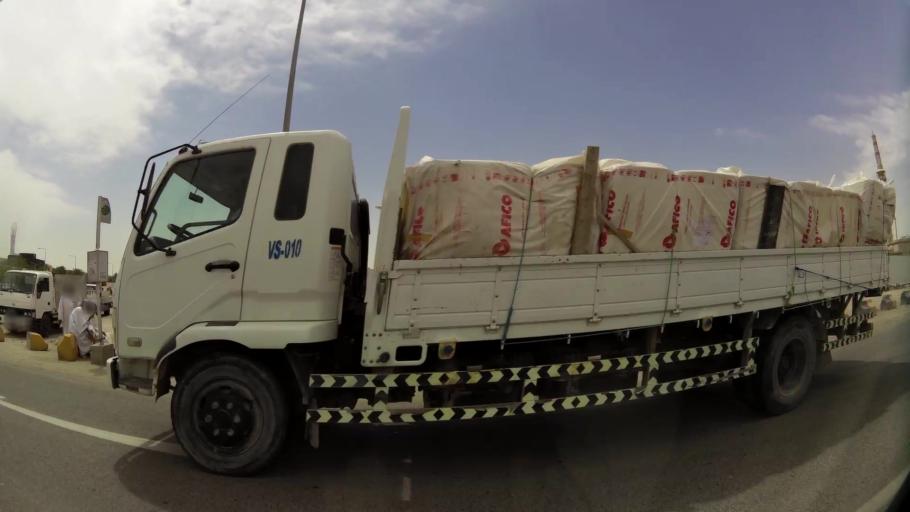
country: QA
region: Baladiyat ar Rayyan
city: Ar Rayyan
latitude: 25.2822
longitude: 51.4344
